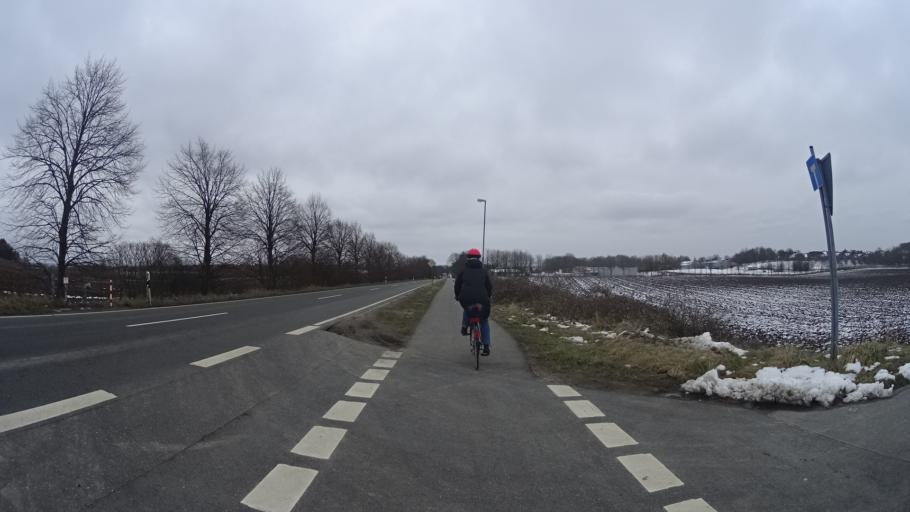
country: DE
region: Schleswig-Holstein
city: Lutjenburg
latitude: 54.3031
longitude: 10.5775
